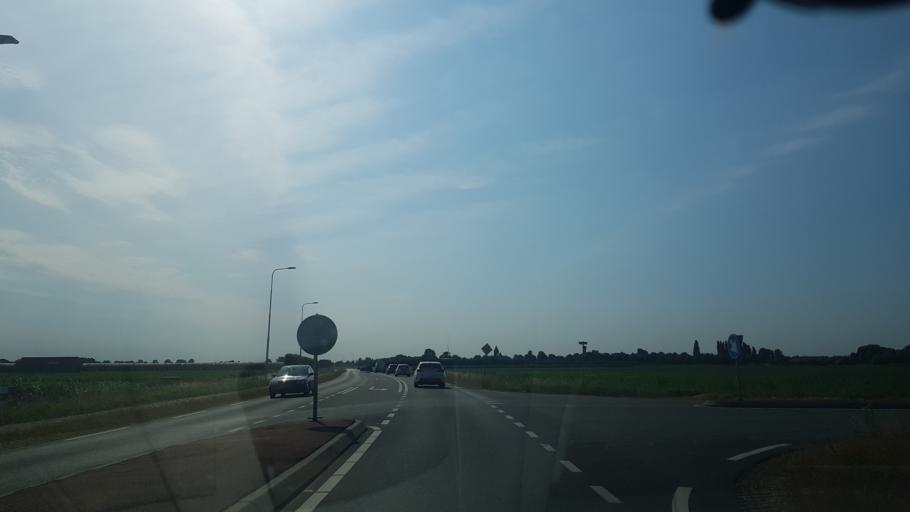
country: NL
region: Zeeland
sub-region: Gemeente Tholen
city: Tholen
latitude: 51.5424
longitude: 4.1611
